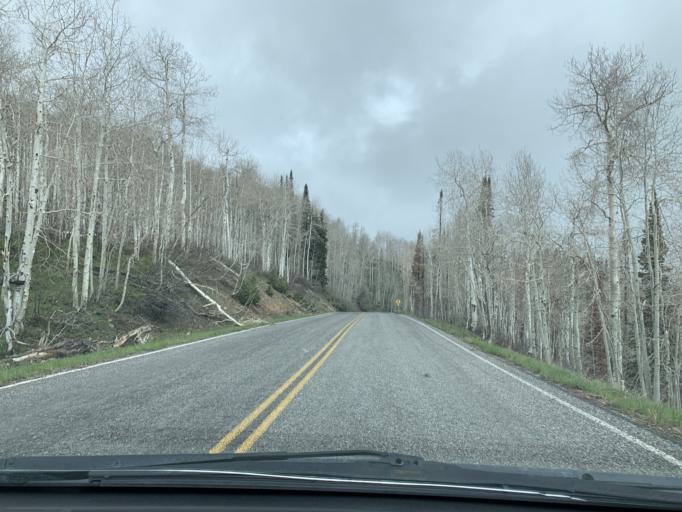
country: US
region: Utah
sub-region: Utah County
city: Elk Ridge
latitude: 39.8793
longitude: -111.6857
